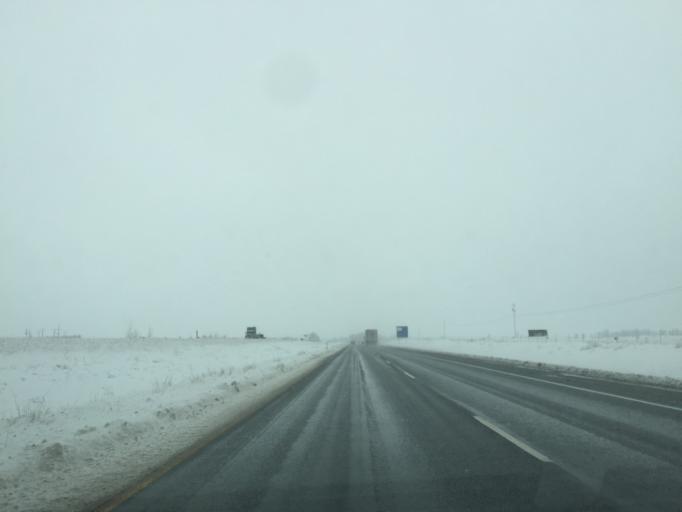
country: US
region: Washington
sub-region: Spokane County
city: Airway Heights
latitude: 47.5997
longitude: -117.5492
